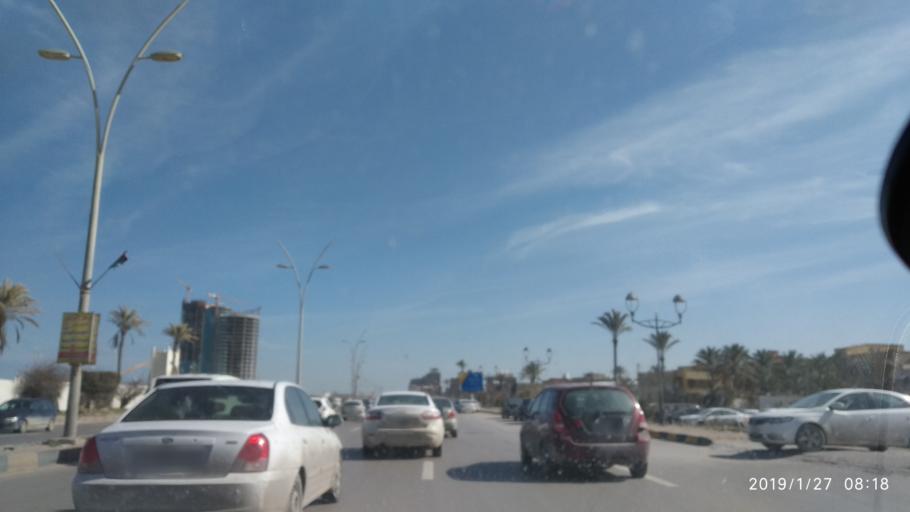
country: LY
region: Tripoli
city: Tripoli
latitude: 32.9066
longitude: 13.2583
